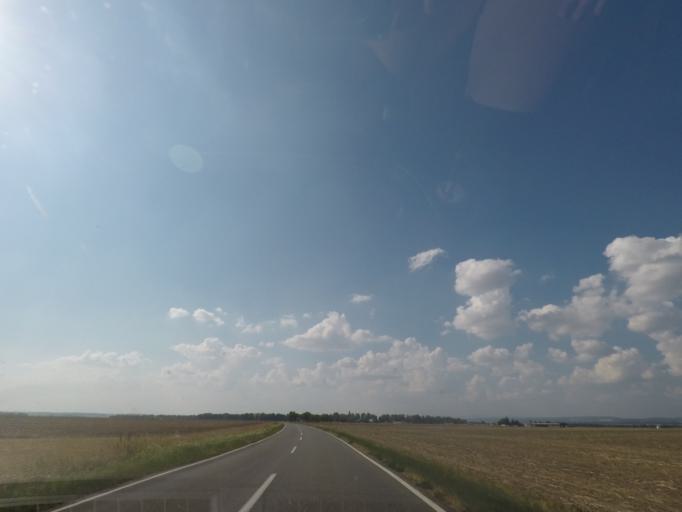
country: CZ
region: Kralovehradecky
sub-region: Okres Nachod
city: Jaromer
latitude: 50.3276
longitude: 15.9477
